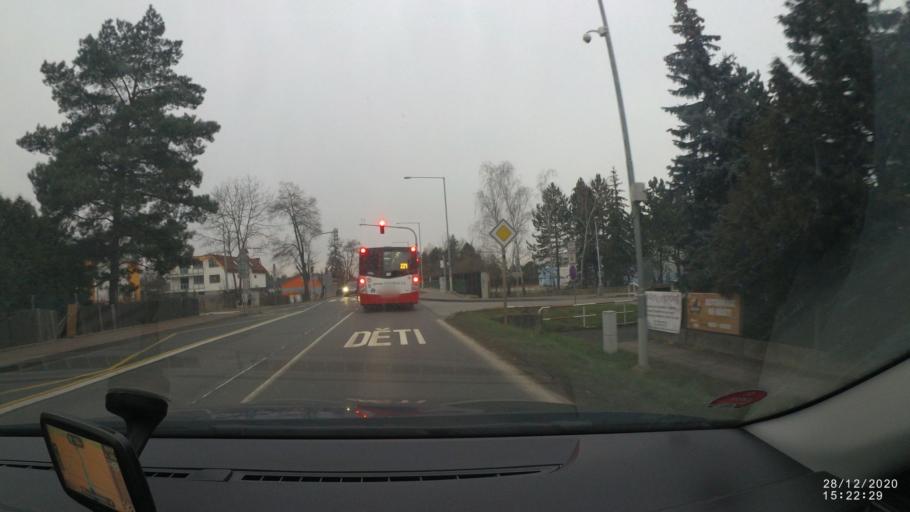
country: CZ
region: Central Bohemia
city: Sestajovice
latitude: 50.0772
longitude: 14.6549
